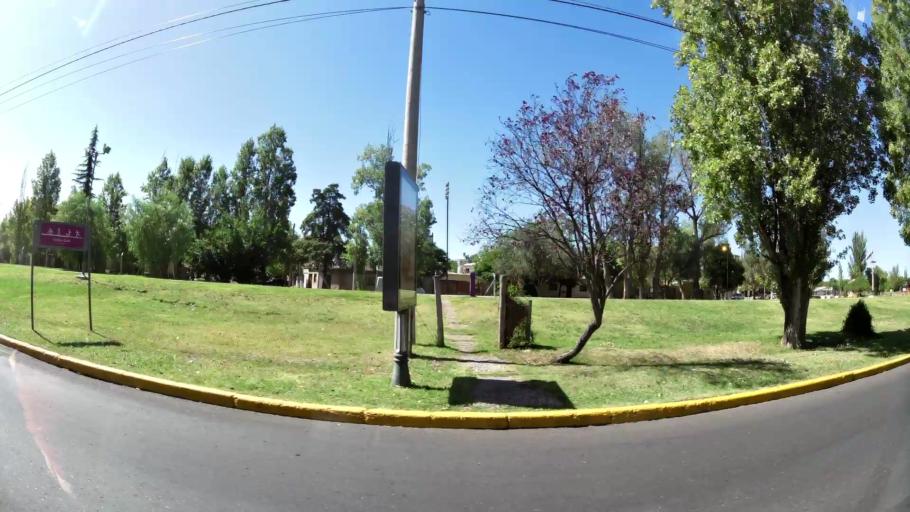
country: AR
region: Mendoza
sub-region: Departamento de Godoy Cruz
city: Godoy Cruz
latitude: -32.9500
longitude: -68.8543
